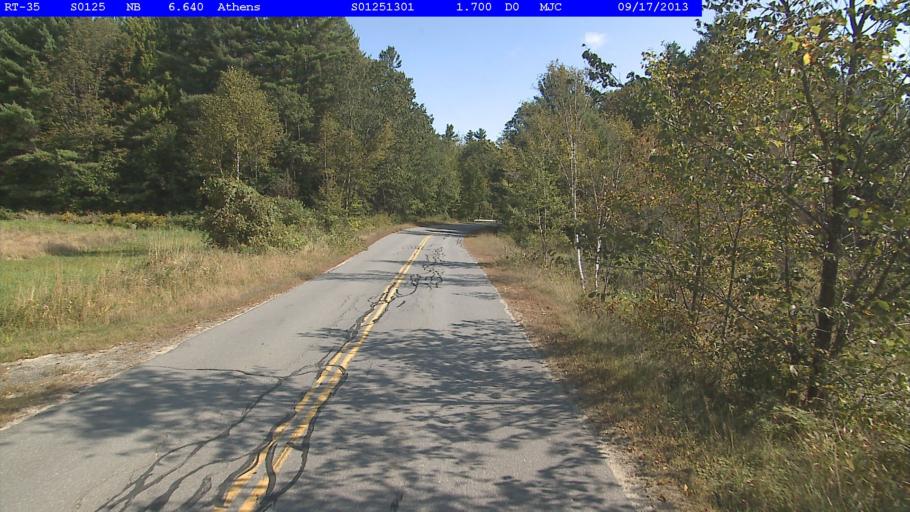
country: US
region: Vermont
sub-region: Windham County
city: Rockingham
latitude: 43.1222
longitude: -72.6000
